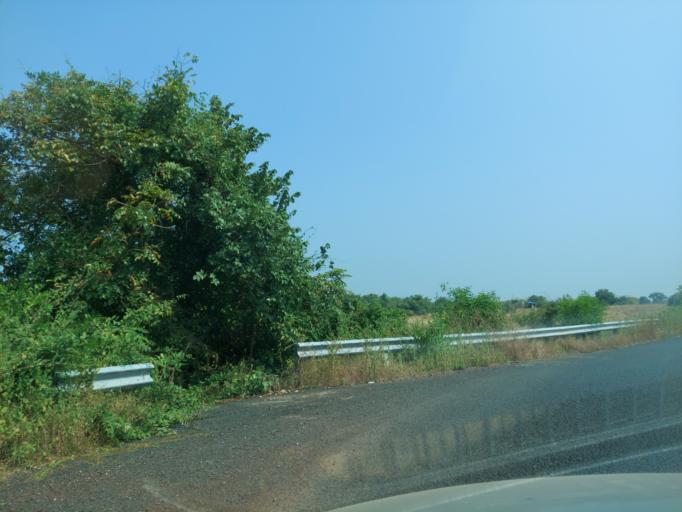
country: IN
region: Maharashtra
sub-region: Sindhudurg
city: Malvan
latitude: 16.0022
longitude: 73.5080
